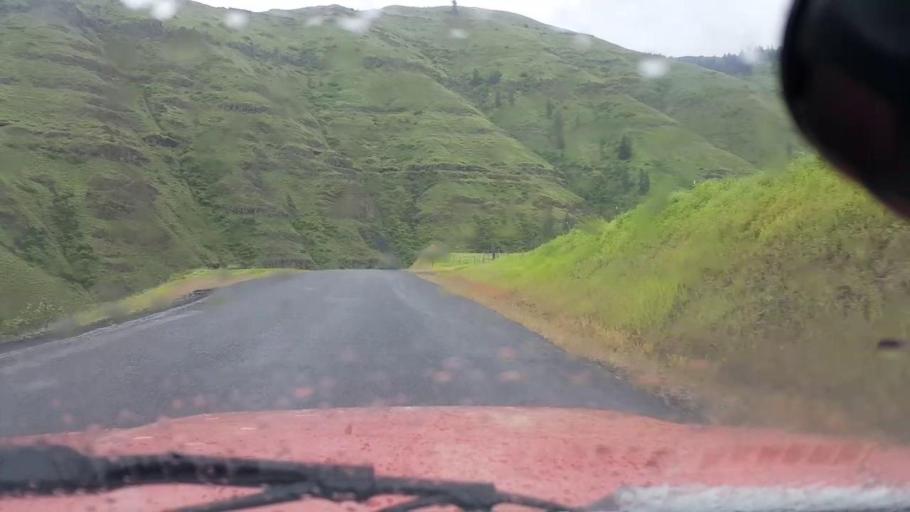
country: US
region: Washington
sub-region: Asotin County
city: Asotin
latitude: 46.0344
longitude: -117.2946
